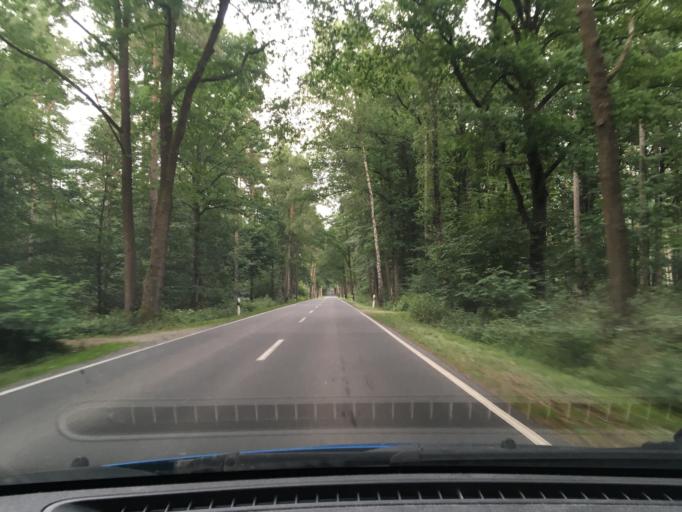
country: DE
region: Lower Saxony
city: Bad Fallingbostel
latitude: 52.8508
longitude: 9.6625
